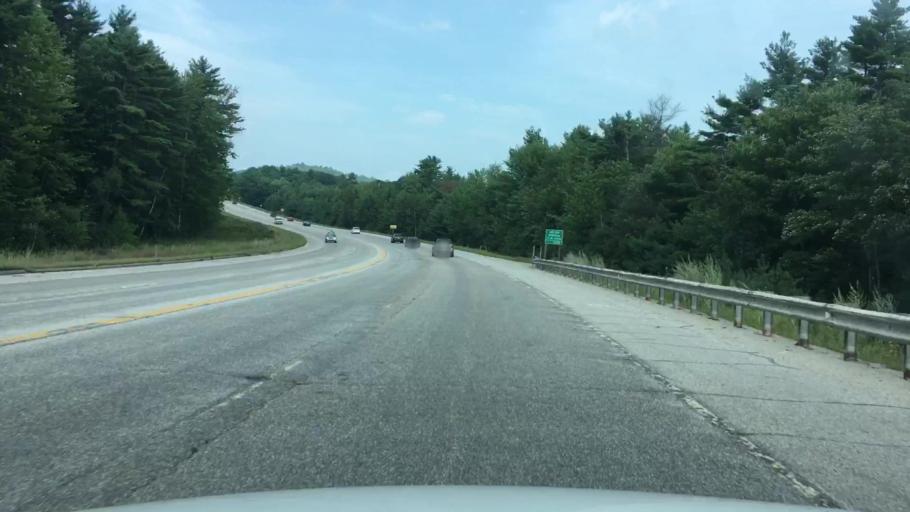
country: US
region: Maine
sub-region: Androscoggin County
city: Lewiston
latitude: 44.1777
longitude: -70.2316
